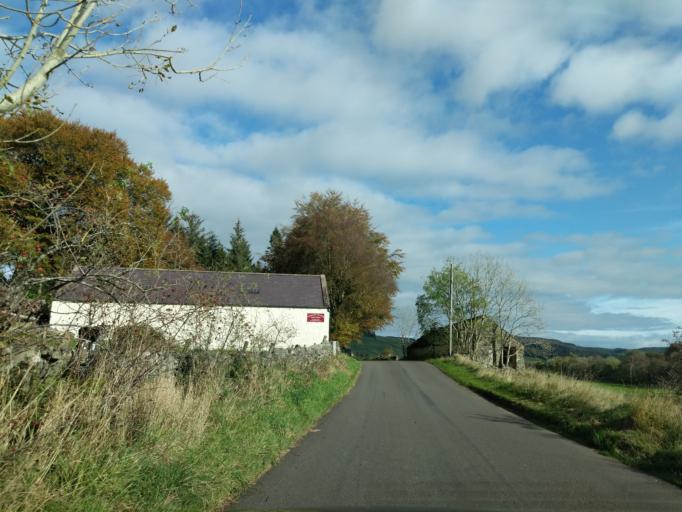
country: GB
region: Scotland
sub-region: Dumfries and Galloway
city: Thornhill
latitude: 55.1870
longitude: -3.9313
